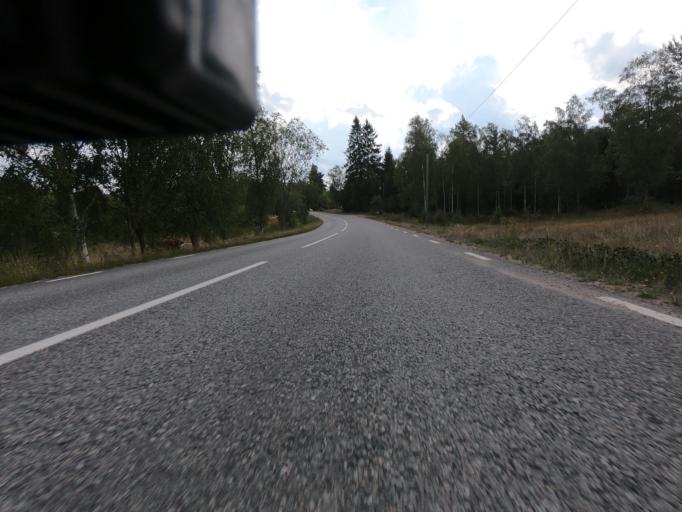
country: SE
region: Joenkoeping
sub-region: Vetlanda Kommun
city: Landsbro
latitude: 57.2869
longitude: 14.8848
